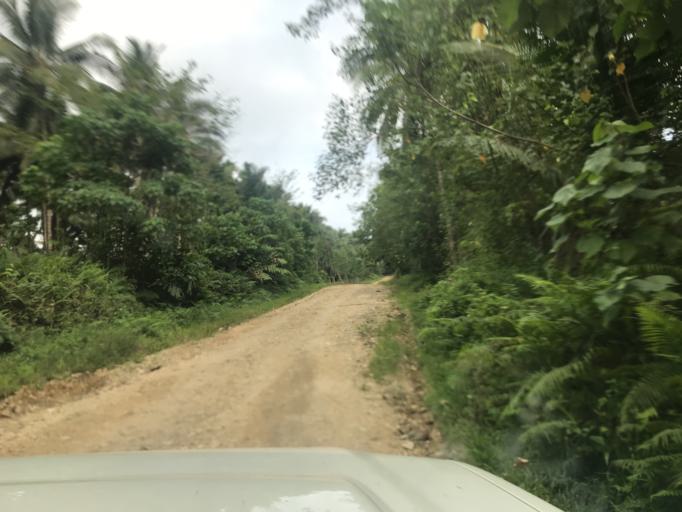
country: VU
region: Sanma
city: Luganville
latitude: -15.5546
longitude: 166.9698
